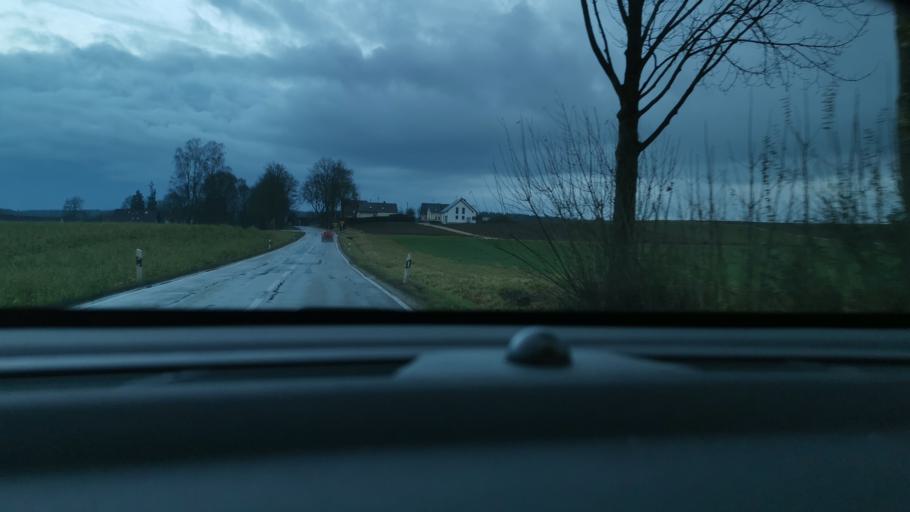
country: DE
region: Bavaria
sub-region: Swabia
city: Aindling
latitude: 48.5601
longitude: 10.9846
